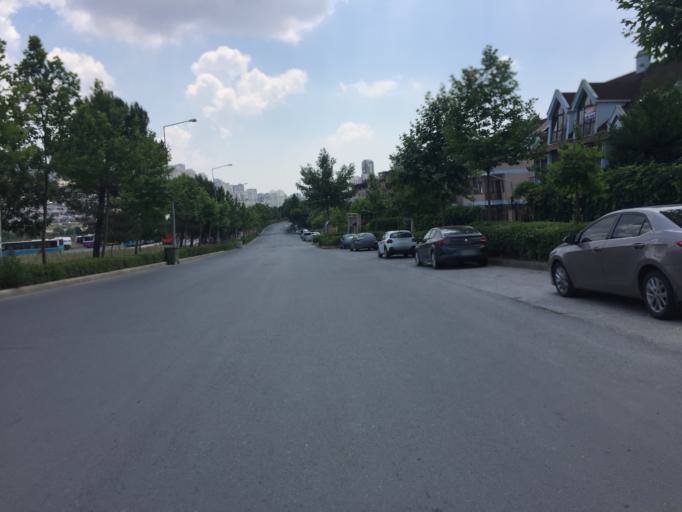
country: TR
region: Istanbul
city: Esenyurt
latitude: 41.0852
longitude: 28.6736
